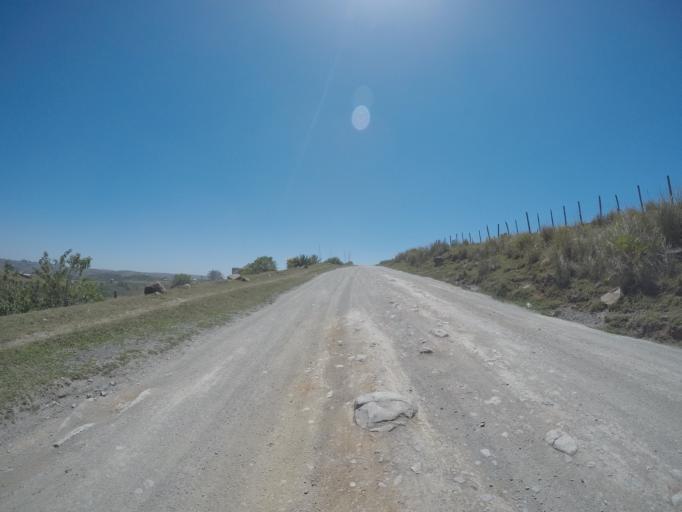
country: ZA
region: Eastern Cape
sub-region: OR Tambo District Municipality
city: Libode
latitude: -32.0103
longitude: 29.0732
